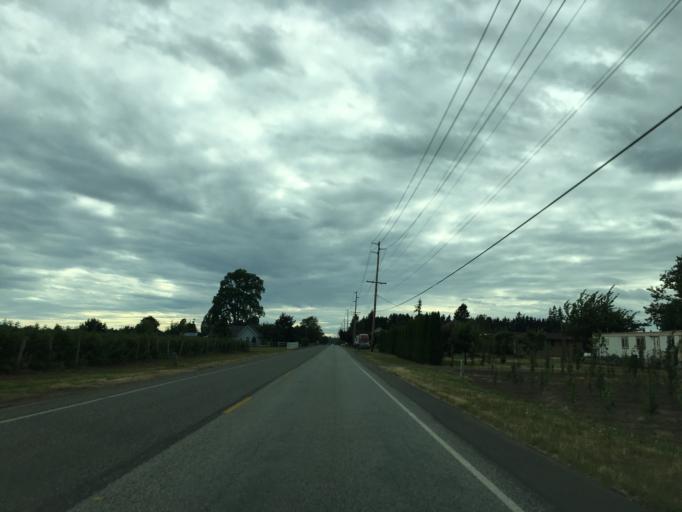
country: US
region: Washington
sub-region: Whatcom County
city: Ferndale
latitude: 48.8880
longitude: -122.5228
